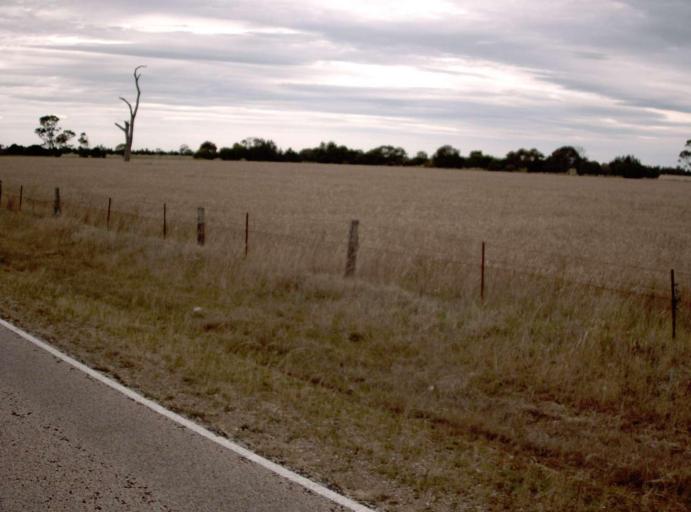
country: AU
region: Victoria
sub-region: East Gippsland
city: Bairnsdale
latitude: -37.9600
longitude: 147.4971
